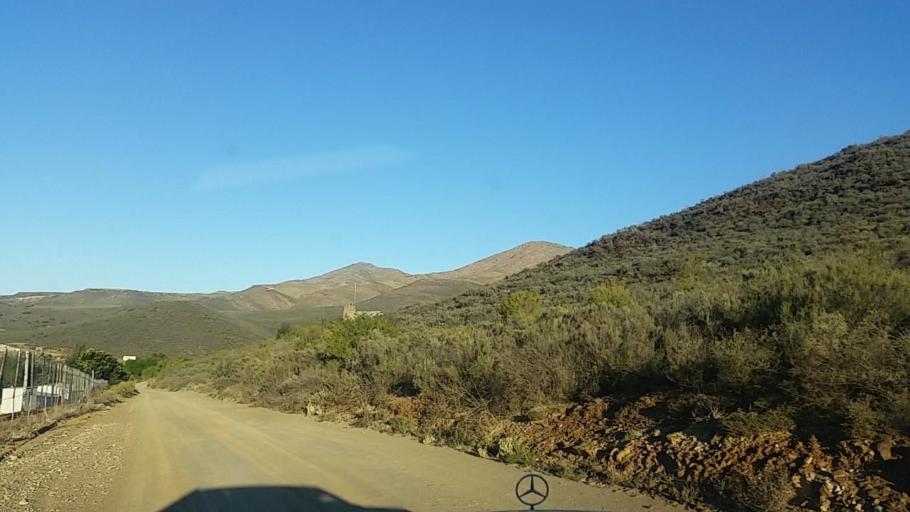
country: ZA
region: Western Cape
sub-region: Eden District Municipality
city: Knysna
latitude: -33.6567
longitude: 23.1343
